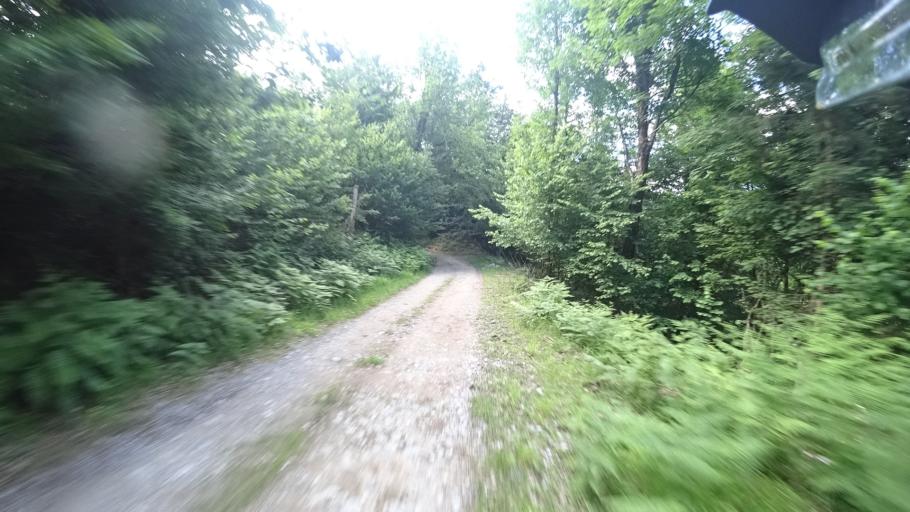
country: SI
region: Osilnica
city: Osilnica
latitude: 45.4648
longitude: 14.7068
